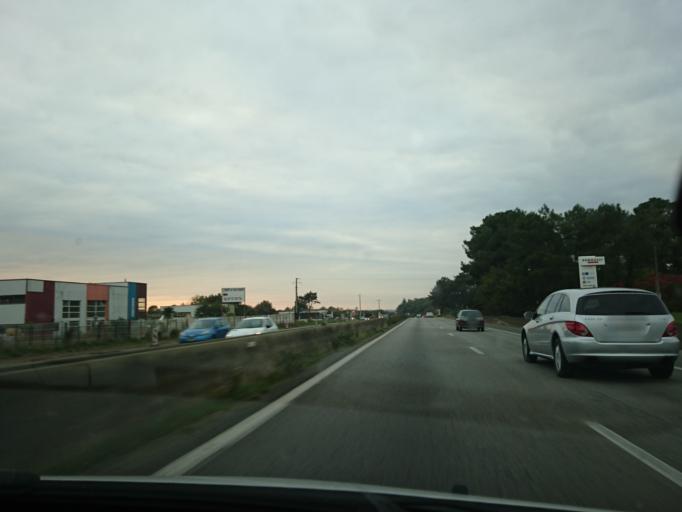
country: FR
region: Brittany
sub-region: Departement du Morbihan
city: Plougoumelen
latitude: 47.6651
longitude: -2.9003
